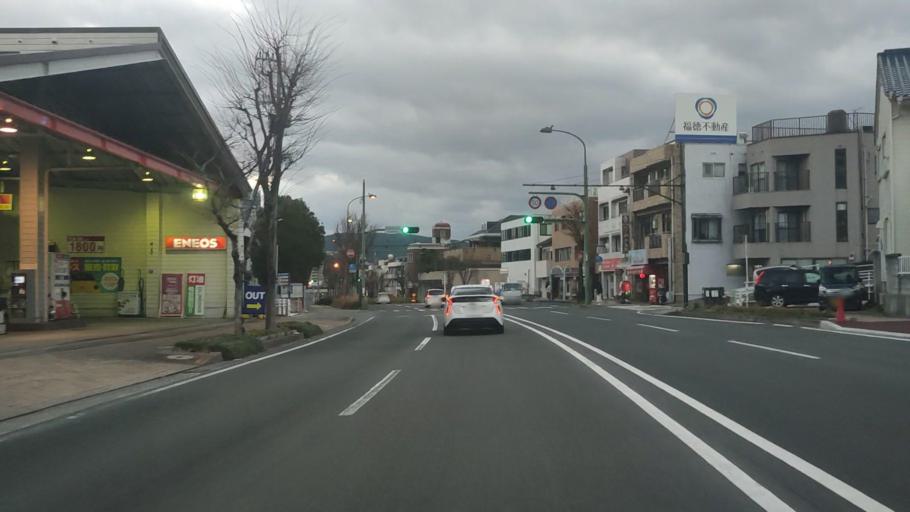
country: JP
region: Nagasaki
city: Nagasaki-shi
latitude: 32.7594
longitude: 129.8869
